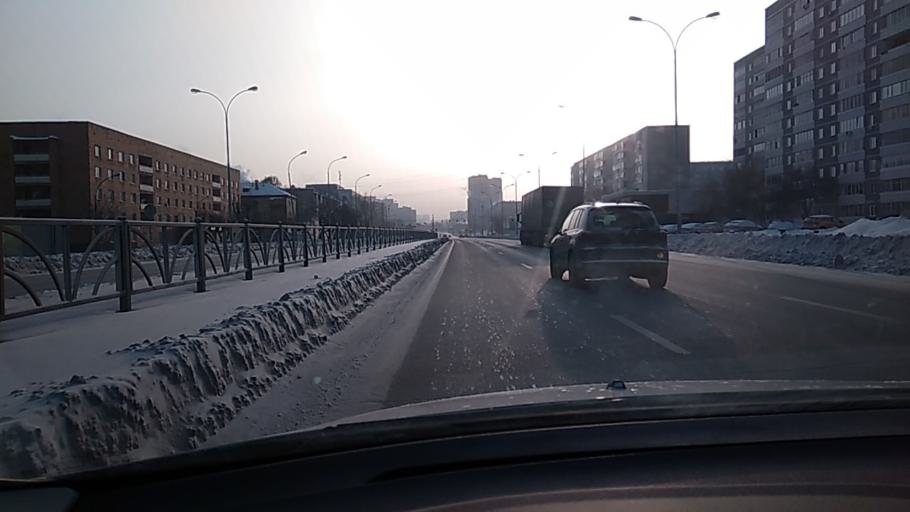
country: RU
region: Sverdlovsk
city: Yekaterinburg
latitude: 56.8134
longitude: 60.6289
